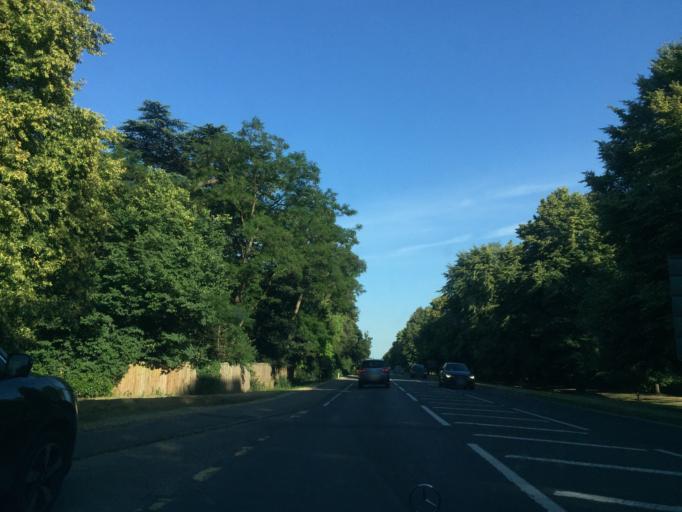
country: GB
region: England
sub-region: Oxfordshire
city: Henley on Thames
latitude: 51.5528
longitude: -0.9236
